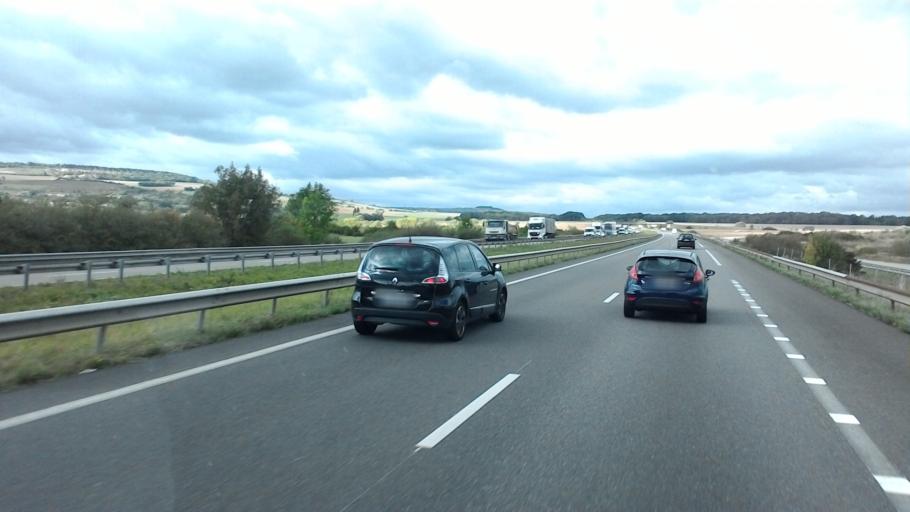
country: FR
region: Lorraine
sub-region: Departement de Meurthe-et-Moselle
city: Pont-a-Mousson
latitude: 48.9448
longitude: 6.1127
